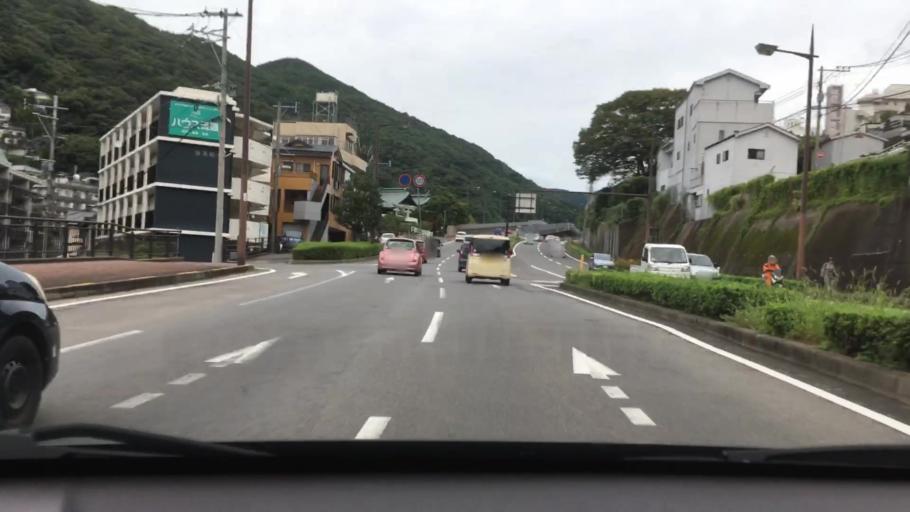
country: JP
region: Nagasaki
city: Nagasaki-shi
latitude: 32.7506
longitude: 129.8962
